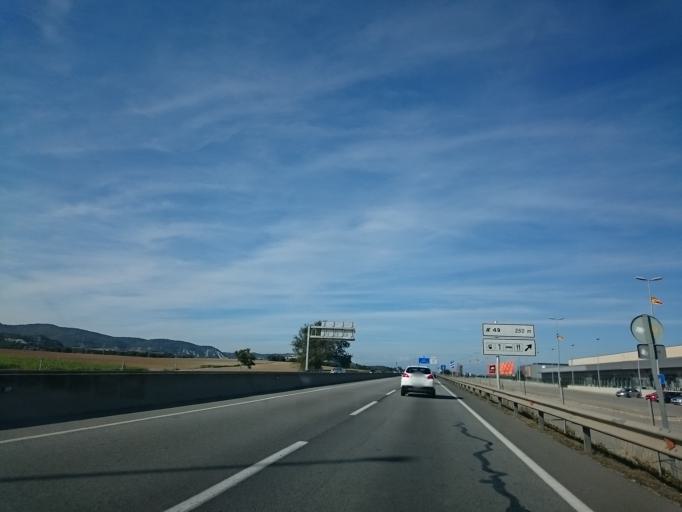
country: ES
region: Catalonia
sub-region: Provincia de Barcelona
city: Tona
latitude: 41.8321
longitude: 2.2343
